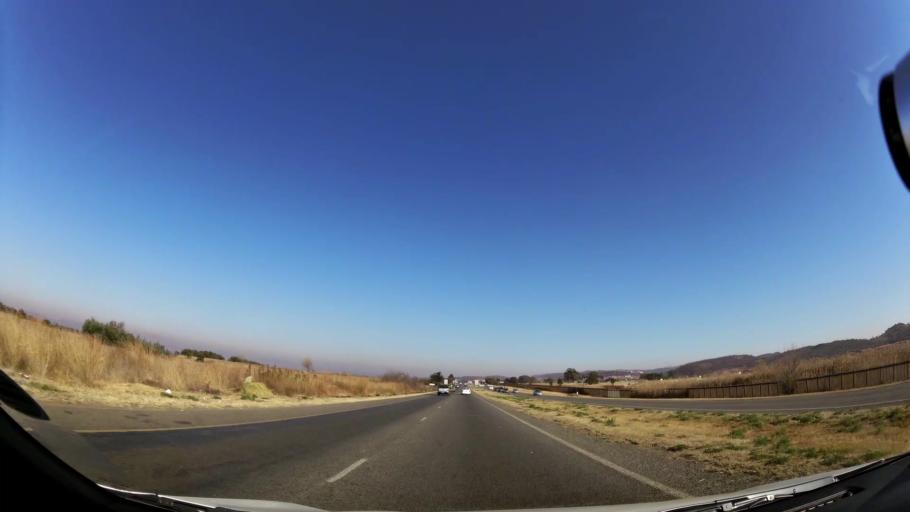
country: ZA
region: Gauteng
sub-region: Ekurhuleni Metropolitan Municipality
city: Germiston
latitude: -26.3122
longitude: 28.0878
